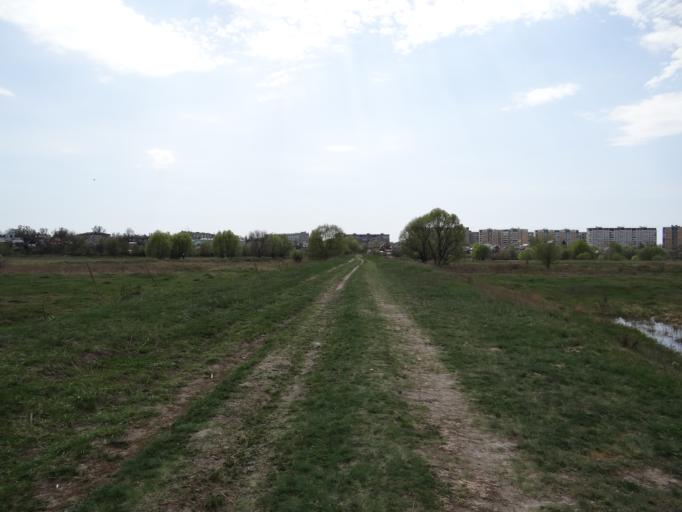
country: RU
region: Kursk
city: Voroshnevo
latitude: 51.6758
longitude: 36.0806
